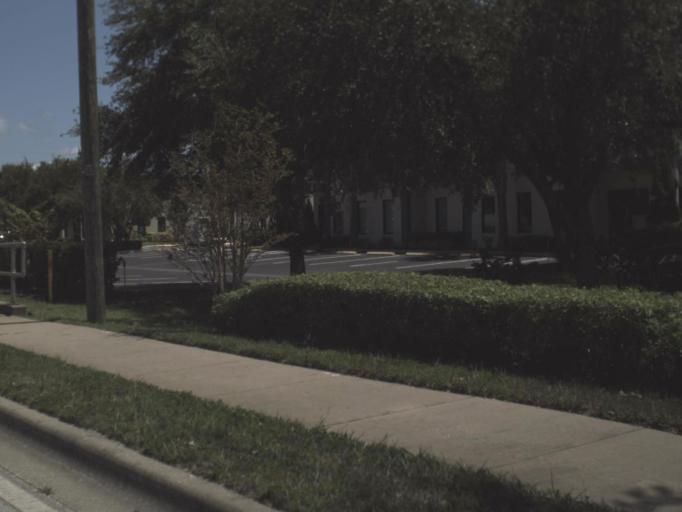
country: US
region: Florida
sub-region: Pinellas County
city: Pinellas Park
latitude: 27.8791
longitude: -82.6943
